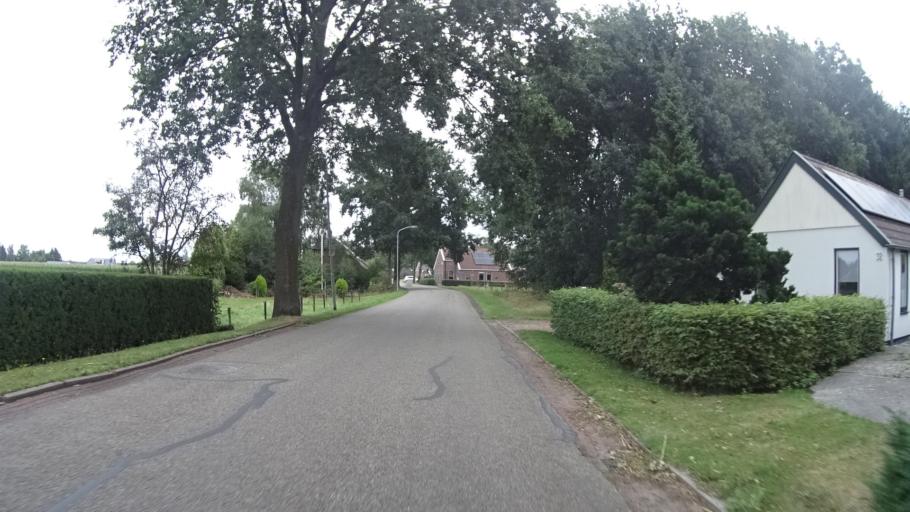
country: NL
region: Groningen
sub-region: Gemeente Slochteren
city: Slochteren
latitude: 53.2260
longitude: 6.7993
